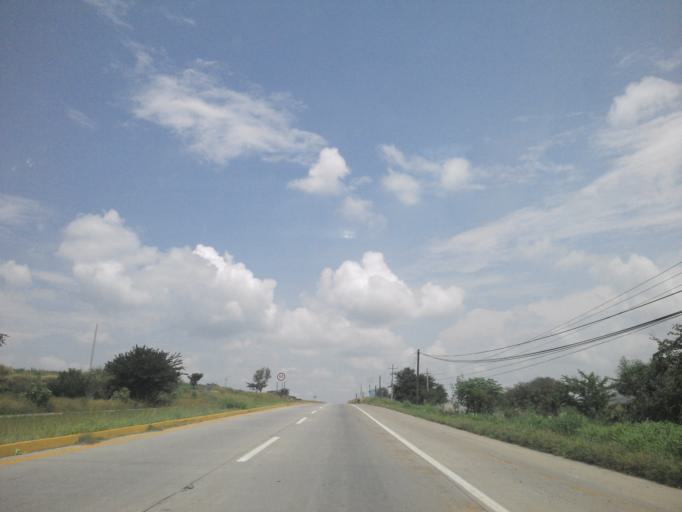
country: MX
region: Jalisco
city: Zapotlanejo
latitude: 20.6019
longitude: -103.0972
